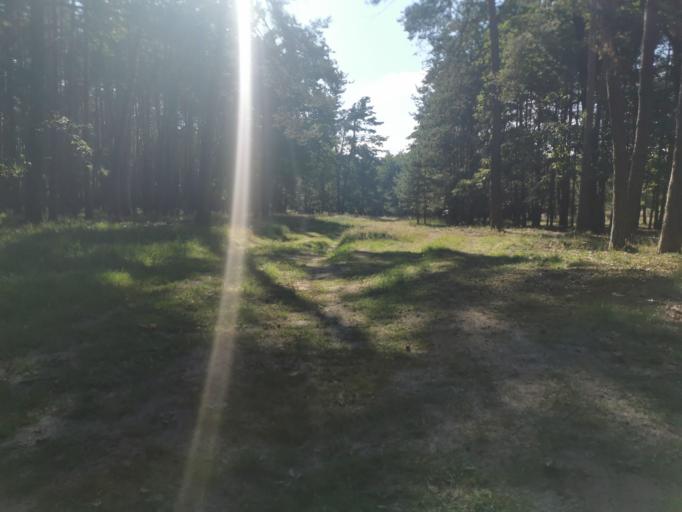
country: SK
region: Trnavsky
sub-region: Okres Senica
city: Senica
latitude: 48.6041
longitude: 17.2657
